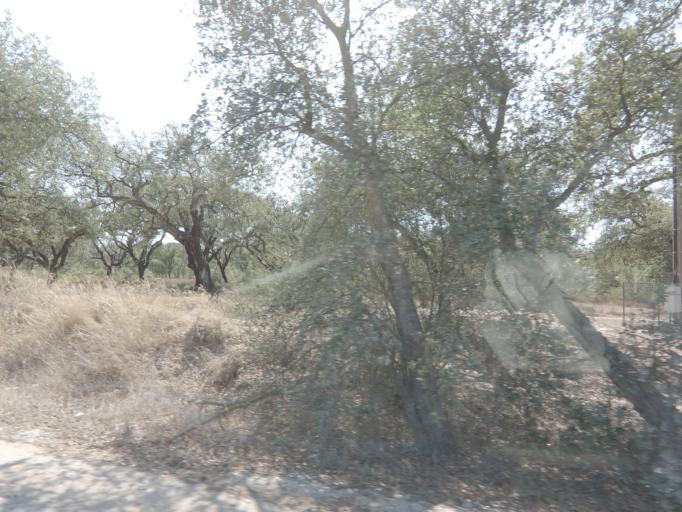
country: PT
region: Setubal
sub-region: Palmela
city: Palmela
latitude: 38.5926
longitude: -8.8549
